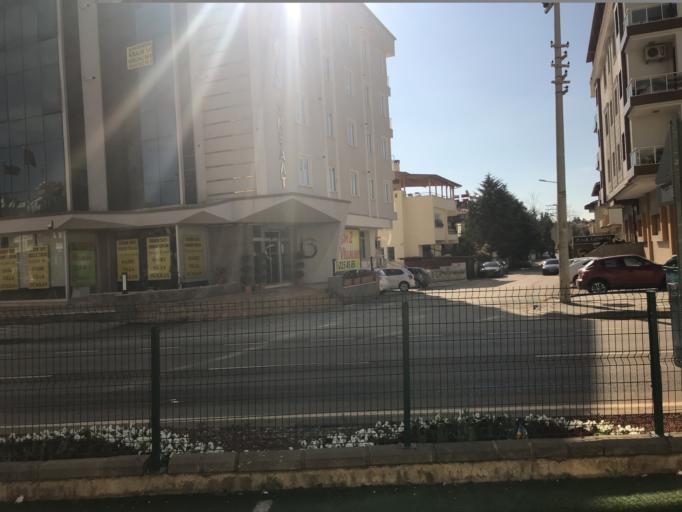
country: TR
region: Gaziantep
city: Sahinbey
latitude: 37.0560
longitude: 37.3305
